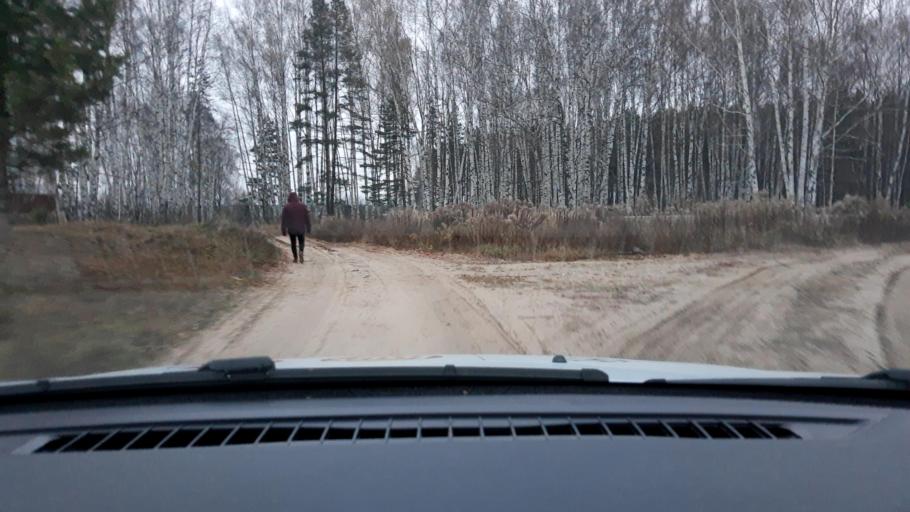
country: RU
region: Nizjnij Novgorod
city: Neklyudovo
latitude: 56.4249
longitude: 44.0107
